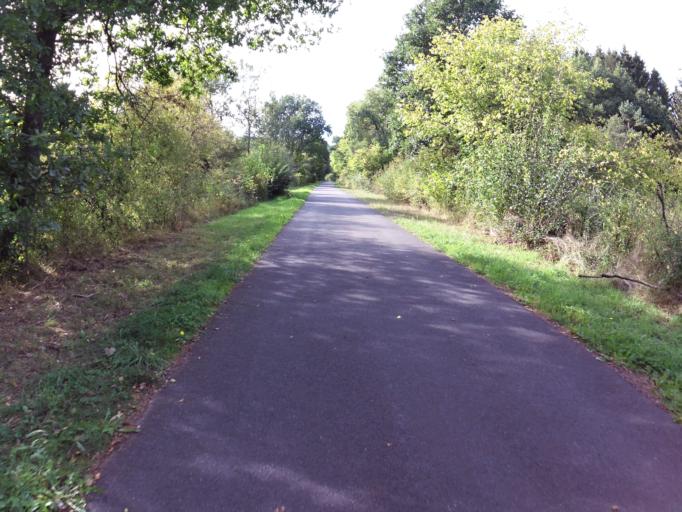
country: DE
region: Rheinland-Pfalz
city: Winterspelt
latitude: 50.2250
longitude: 6.2151
